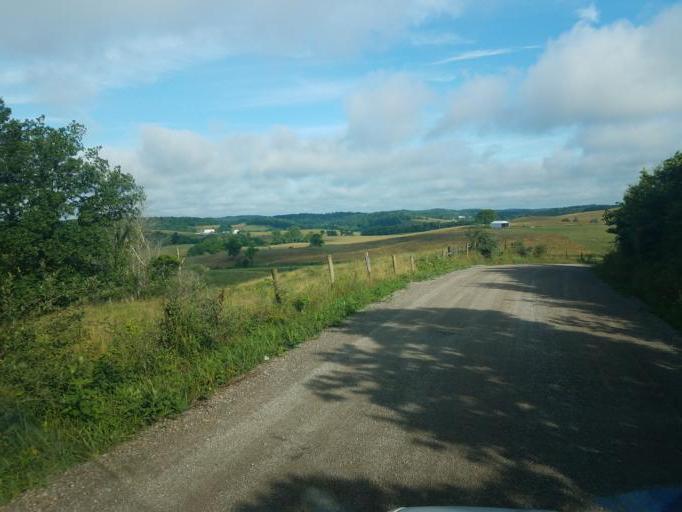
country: US
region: Ohio
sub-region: Gallia County
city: Gallipolis
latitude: 38.7532
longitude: -82.3559
